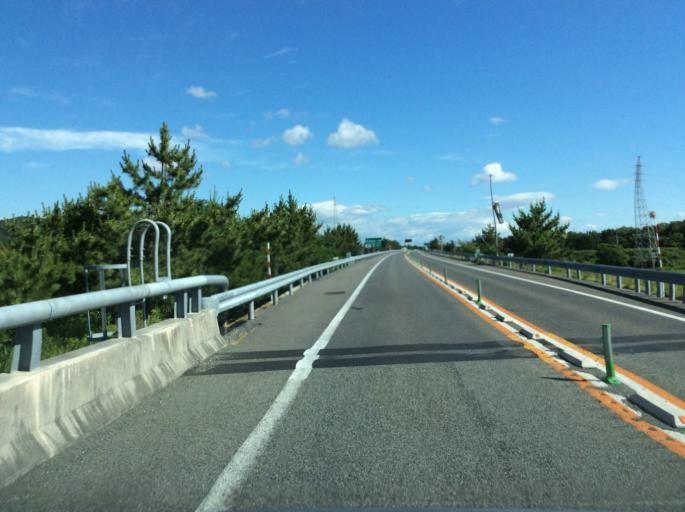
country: JP
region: Fukushima
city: Namie
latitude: 37.3671
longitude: 140.9679
